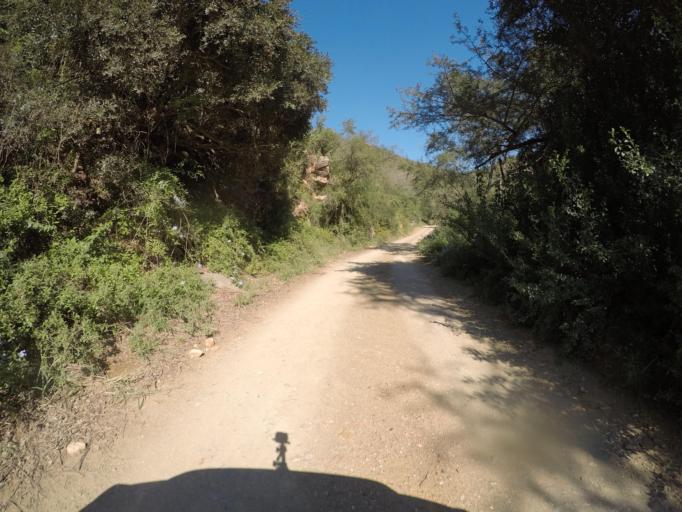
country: ZA
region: Eastern Cape
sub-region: Cacadu District Municipality
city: Kareedouw
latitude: -33.6592
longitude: 24.5281
